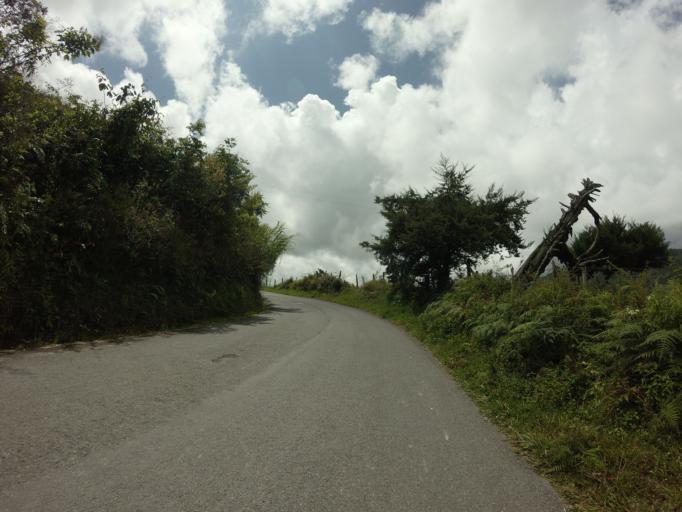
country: CO
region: Caldas
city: Manzanares
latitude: 5.2705
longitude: -75.1413
